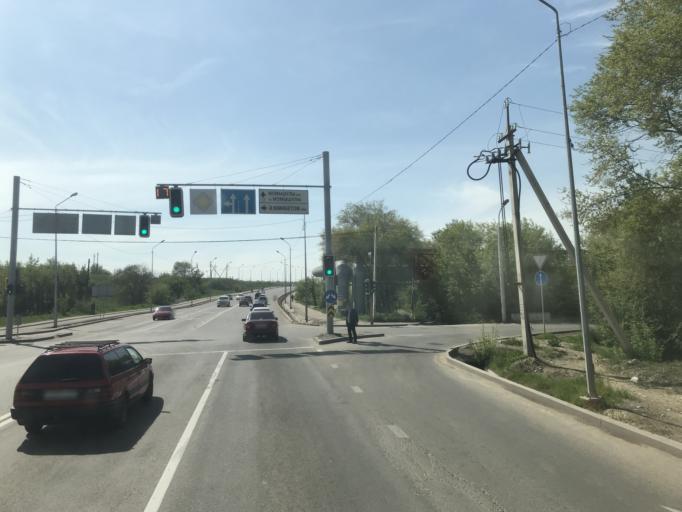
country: KZ
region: Almaty Oblysy
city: Burunday
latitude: 43.3130
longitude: 76.8491
